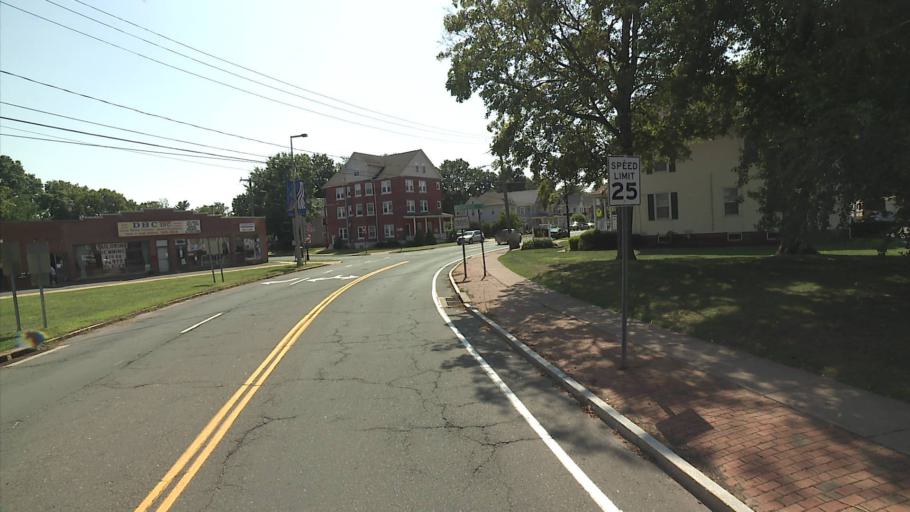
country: US
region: Connecticut
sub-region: Hartford County
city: Windsor
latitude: 41.8531
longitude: -72.6453
